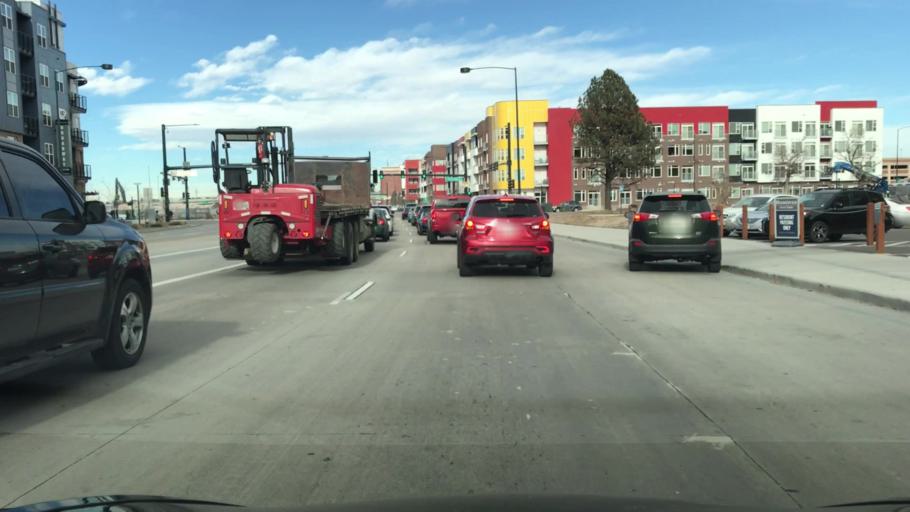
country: US
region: Colorado
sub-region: Denver County
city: Denver
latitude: 39.6956
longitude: -104.9873
